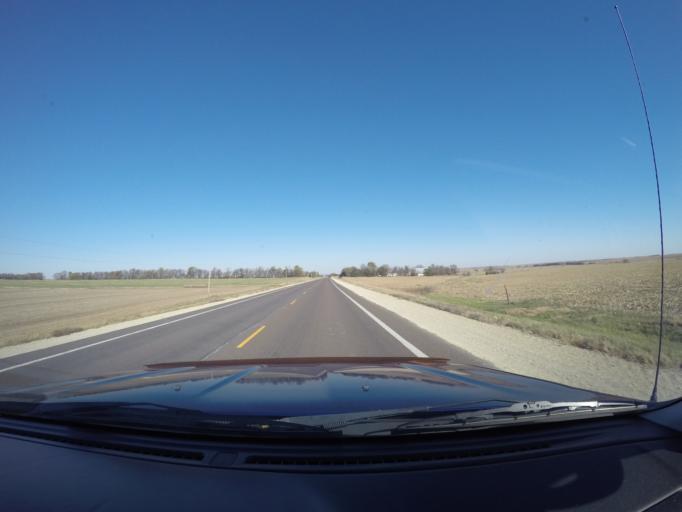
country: US
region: Kansas
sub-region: Marshall County
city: Blue Rapids
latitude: 39.6002
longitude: -96.7502
